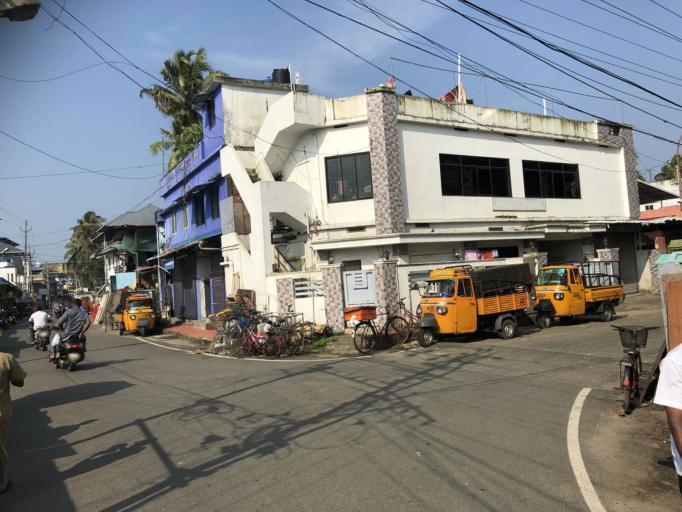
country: IN
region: Kerala
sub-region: Ernakulam
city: Cochin
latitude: 9.9610
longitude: 76.2531
